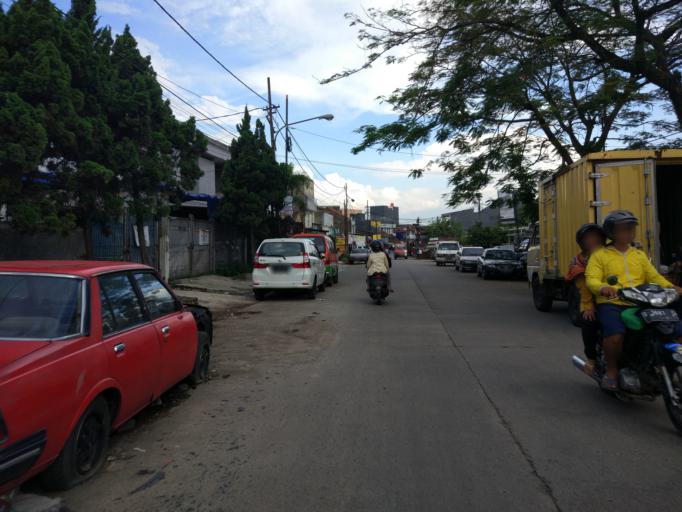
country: ID
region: West Java
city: Bandung
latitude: -6.9224
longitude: 107.5810
